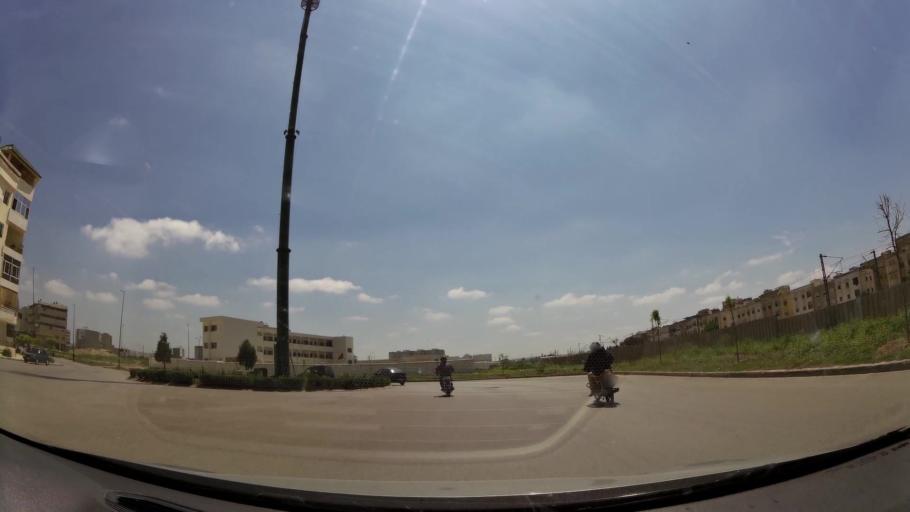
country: MA
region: Fes-Boulemane
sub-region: Fes
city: Fes
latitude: 34.0154
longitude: -5.0445
